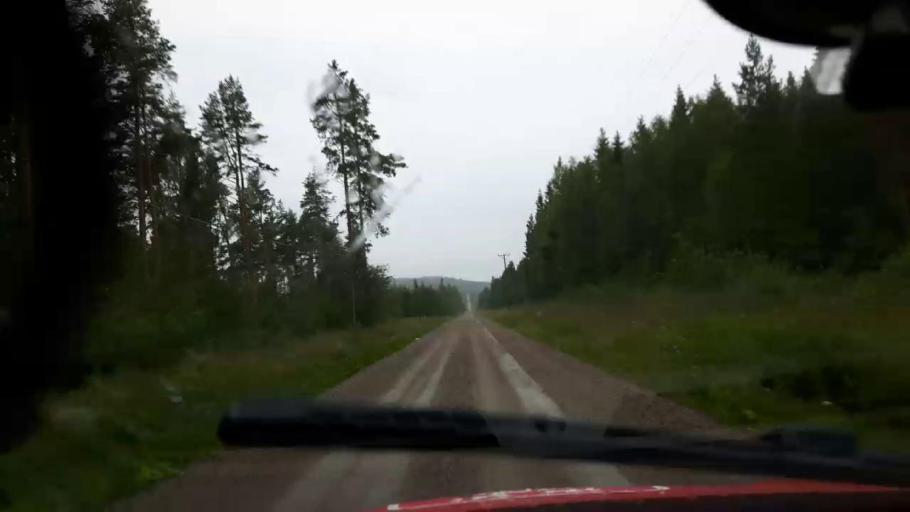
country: SE
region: Jaemtland
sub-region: OEstersunds Kommun
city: Brunflo
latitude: 62.7734
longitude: 14.9930
